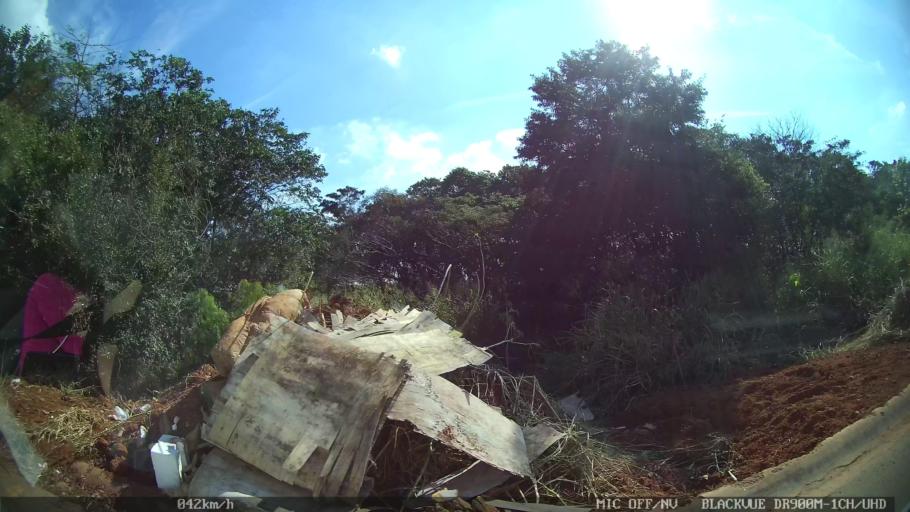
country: BR
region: Sao Paulo
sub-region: Hortolandia
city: Hortolandia
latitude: -22.8661
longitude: -47.2381
